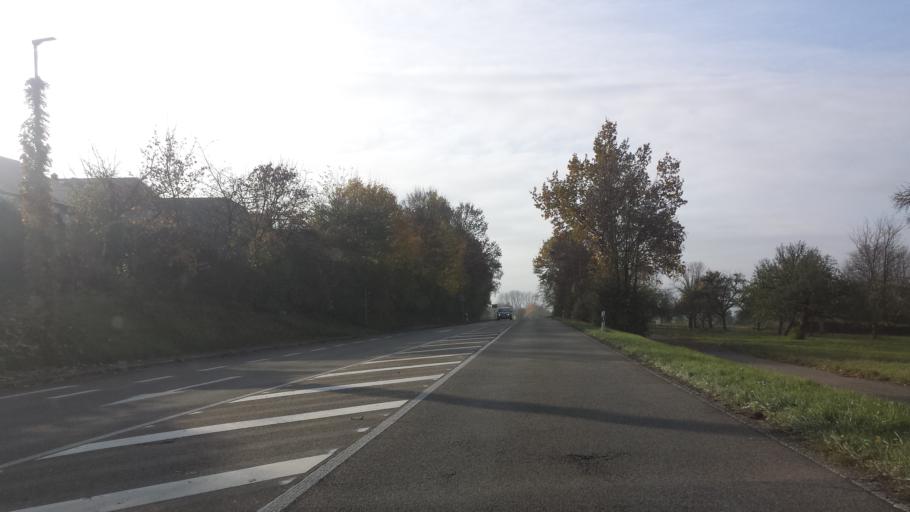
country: DE
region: Baden-Wuerttemberg
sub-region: Karlsruhe Region
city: Ubstadt-Weiher
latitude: 49.1772
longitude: 8.6420
